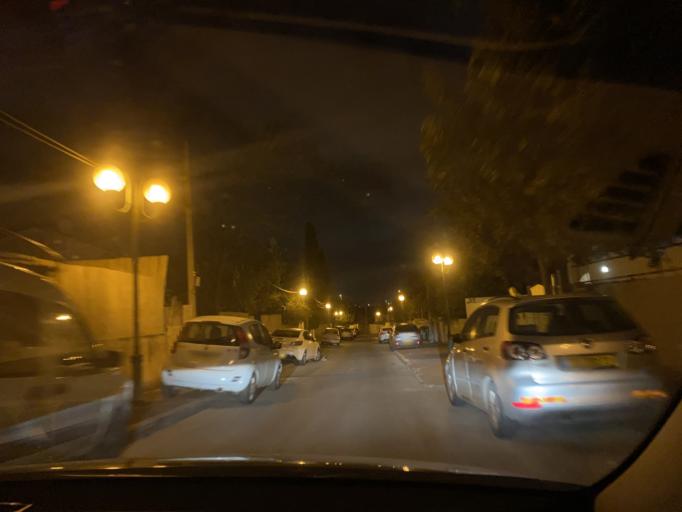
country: IL
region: Central District
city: Kfar Saba
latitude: 32.1571
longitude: 34.9221
